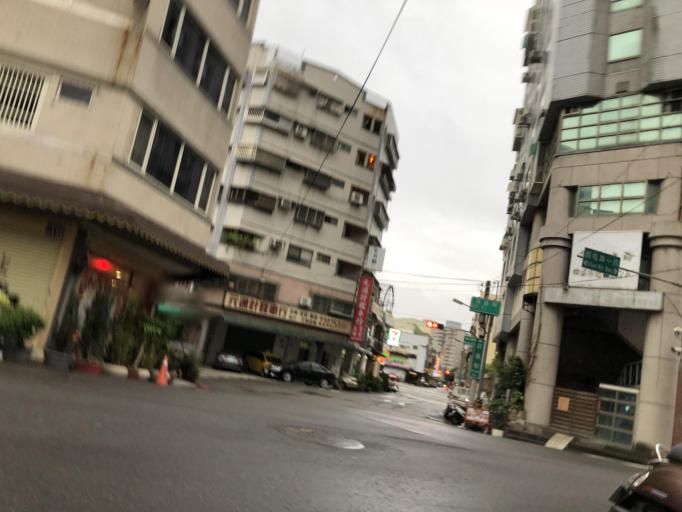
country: TW
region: Taiwan
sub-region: Taichung City
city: Taichung
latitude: 24.1516
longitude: 120.6718
